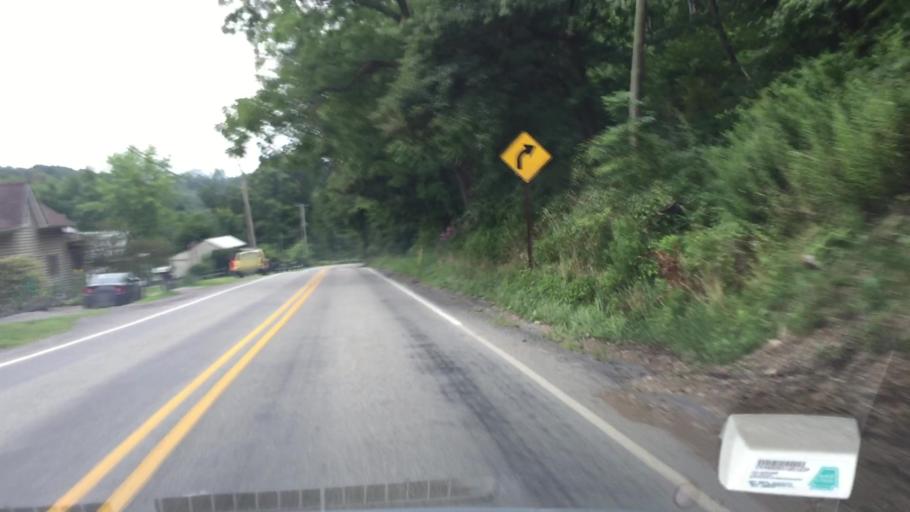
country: US
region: Pennsylvania
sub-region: Allegheny County
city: Curtisville
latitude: 40.6784
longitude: -79.8297
